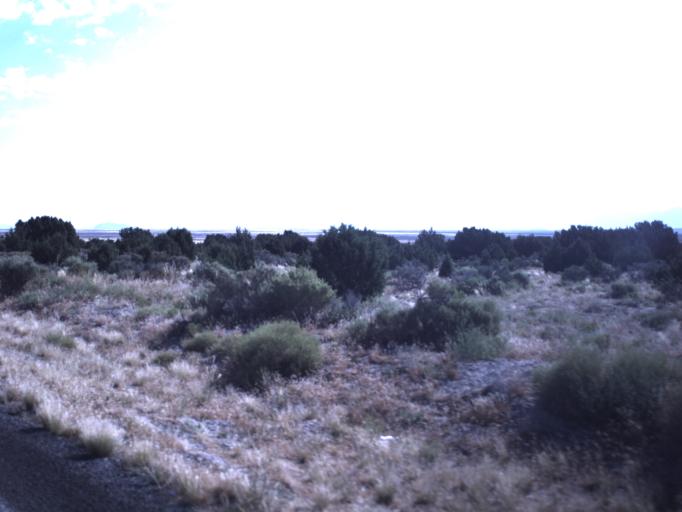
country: US
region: Utah
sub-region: Beaver County
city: Milford
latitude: 38.8366
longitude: -112.8470
